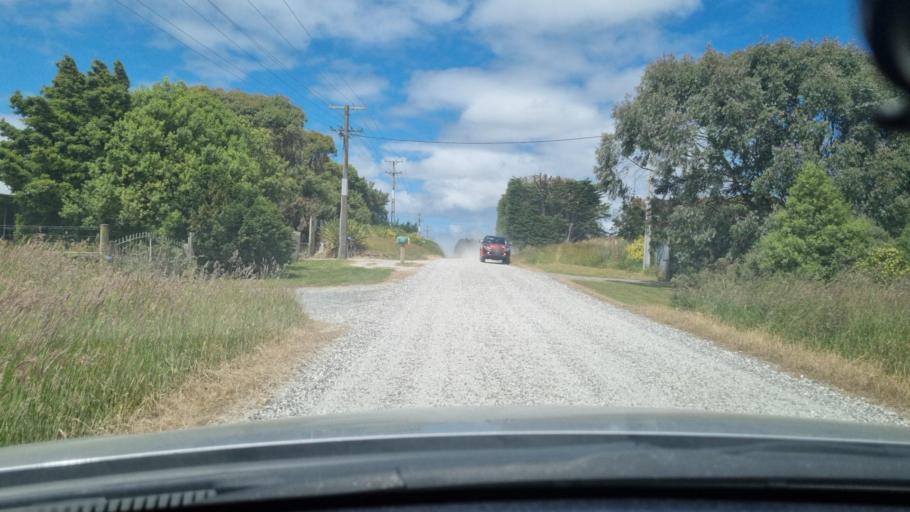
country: NZ
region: Southland
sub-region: Invercargill City
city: Invercargill
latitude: -46.4491
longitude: 168.3034
